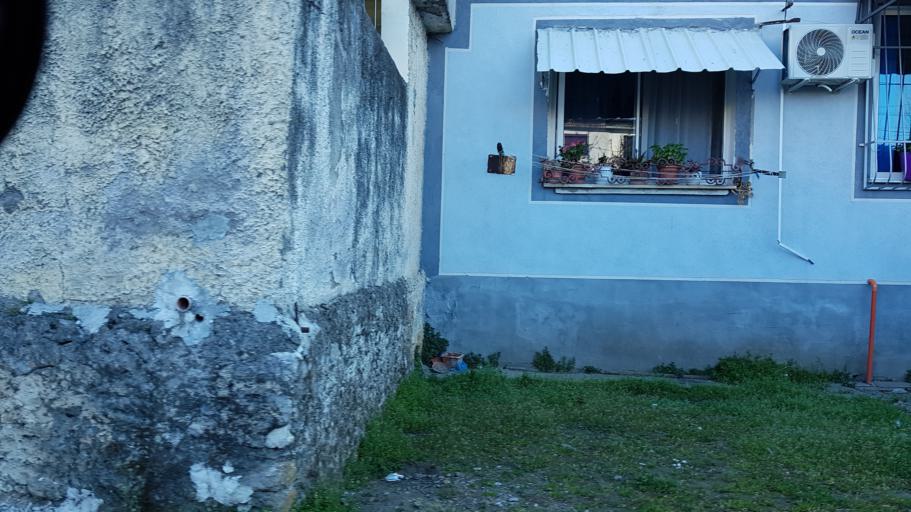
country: AL
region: Shkoder
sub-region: Rrethi i Shkodres
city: Shkoder
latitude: 42.0589
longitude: 19.5146
